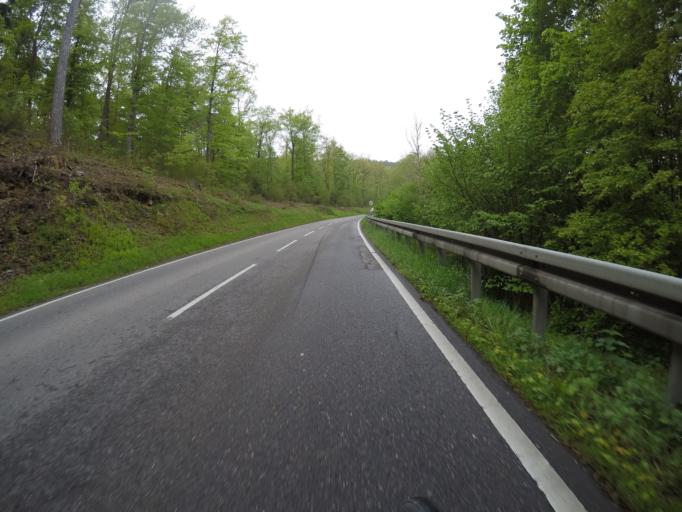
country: DE
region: Baden-Wuerttemberg
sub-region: Regierungsbezirk Stuttgart
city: Weil der Stadt
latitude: 48.7663
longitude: 8.8991
